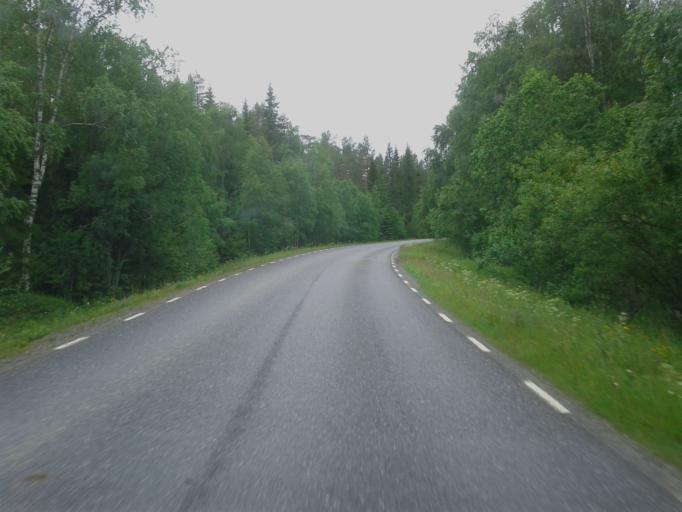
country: SE
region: Vaesterbotten
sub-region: Skelleftea Kommun
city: Forsbacka
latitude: 64.8960
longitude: 20.6945
